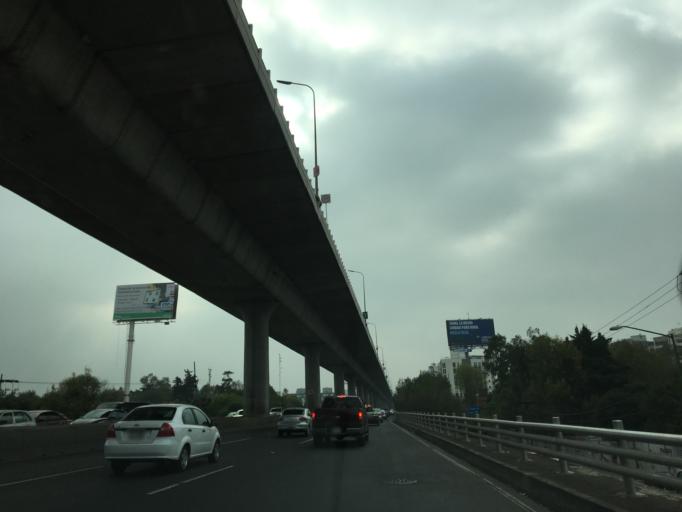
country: MX
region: Mexico City
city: Tlalpan
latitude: 19.2987
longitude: -99.1581
